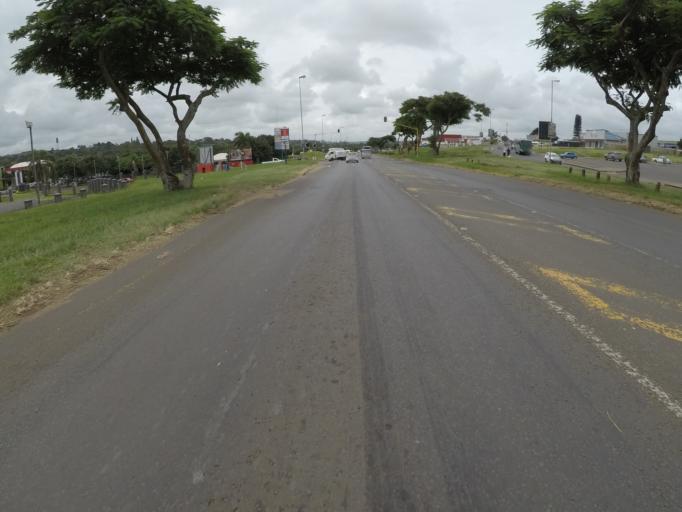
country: ZA
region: KwaZulu-Natal
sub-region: uThungulu District Municipality
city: Empangeni
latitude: -28.7751
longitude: 31.9008
